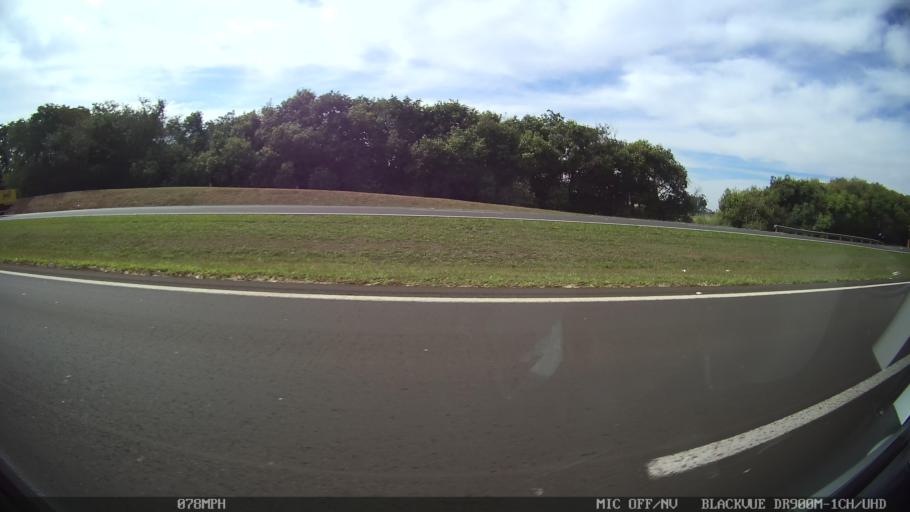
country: BR
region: Sao Paulo
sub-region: Matao
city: Matao
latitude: -21.6184
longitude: -48.4160
